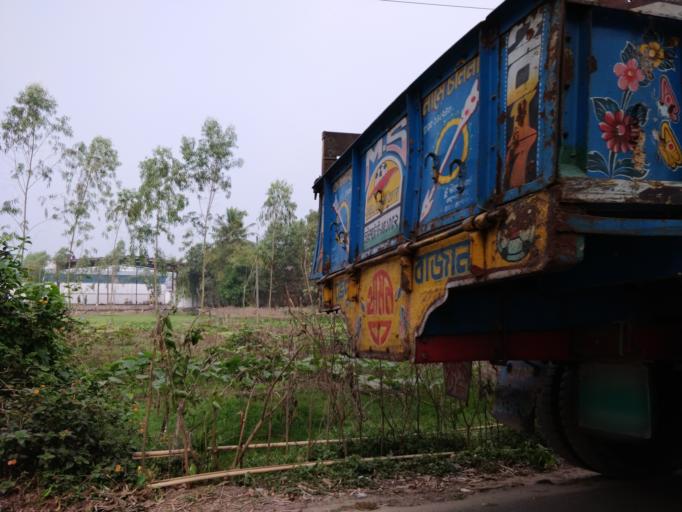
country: BD
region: Sylhet
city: Habiganj
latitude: 24.1700
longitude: 91.3550
